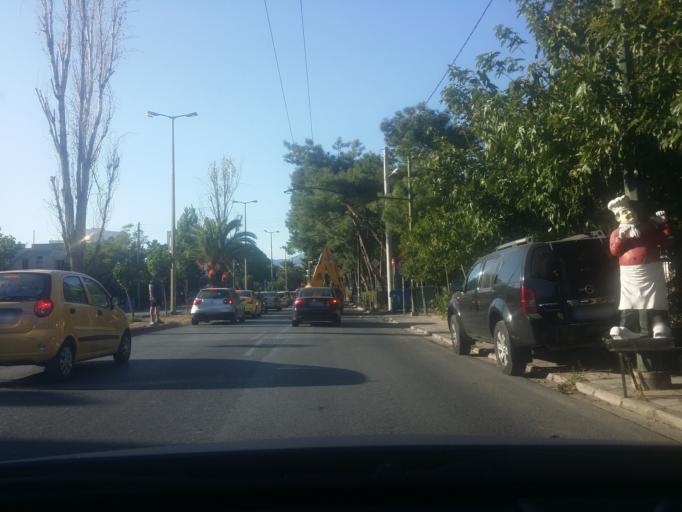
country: GR
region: Attica
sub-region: Nomarchia Athinas
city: Khalandrion
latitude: 38.0193
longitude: 23.7948
